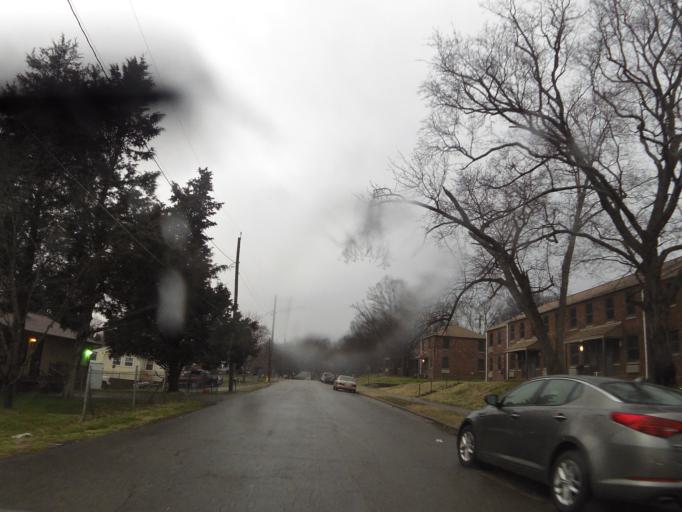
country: US
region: Tennessee
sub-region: Knox County
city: Knoxville
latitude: 35.9746
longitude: -83.9507
